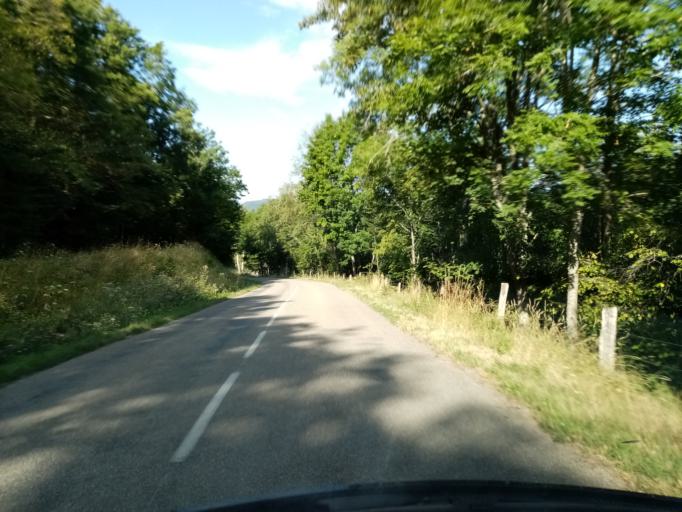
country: FR
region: Alsace
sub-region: Departement du Bas-Rhin
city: Ville
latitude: 48.3505
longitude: 7.3381
